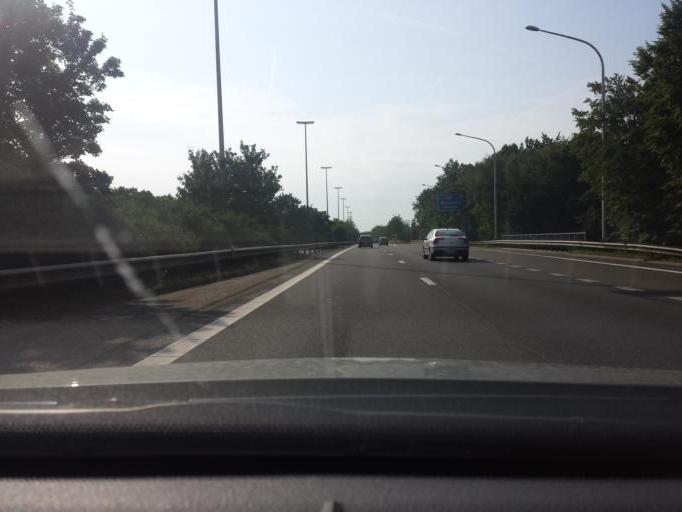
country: BE
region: Flanders
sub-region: Provincie Limburg
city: Hasselt
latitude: 50.9053
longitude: 5.3485
